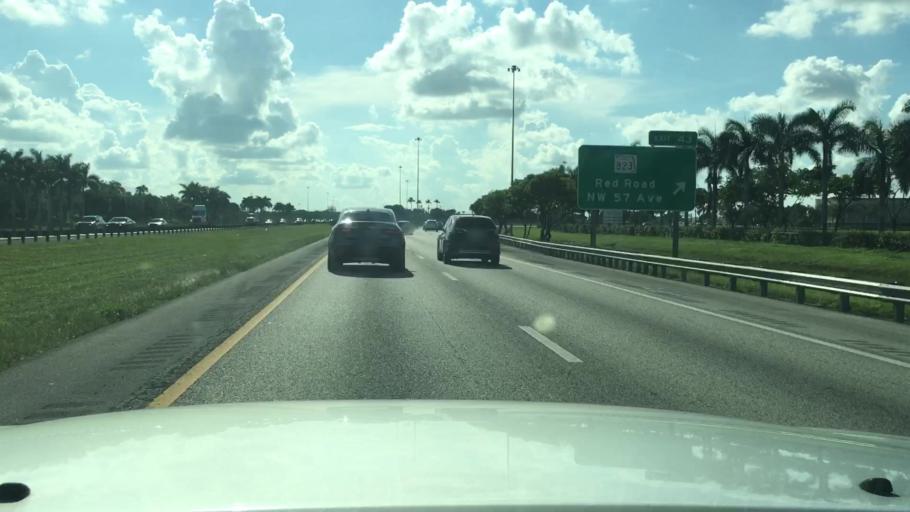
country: US
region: Florida
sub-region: Miami-Dade County
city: Country Club
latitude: 25.9714
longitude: -80.2877
